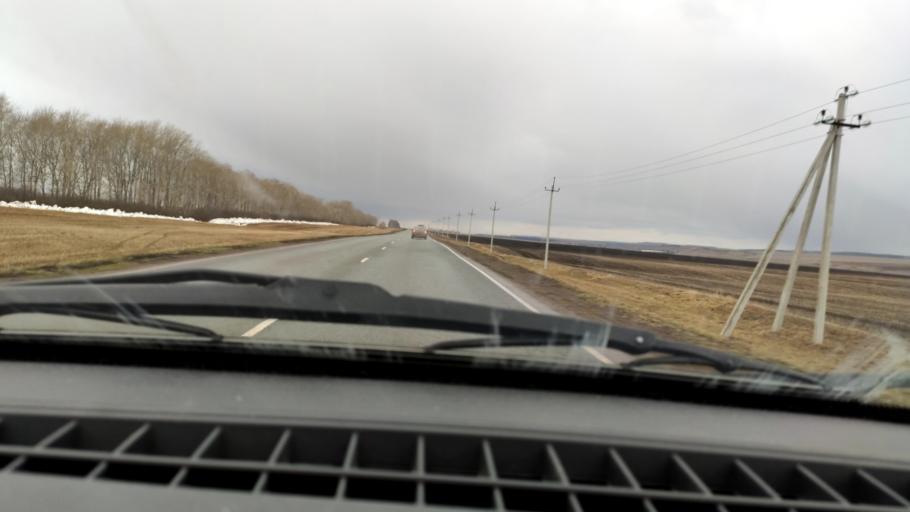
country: RU
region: Bashkortostan
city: Chekmagush
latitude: 55.1136
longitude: 54.8819
